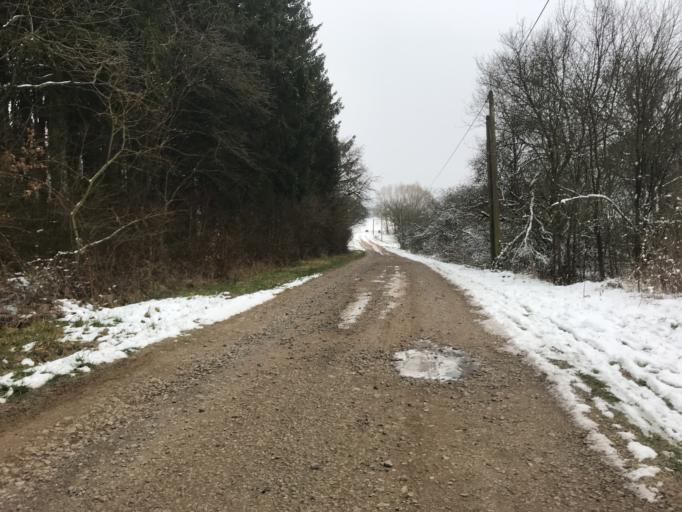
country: FR
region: Lorraine
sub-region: Departement de la Moselle
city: Russange
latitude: 49.4942
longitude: 5.9418
